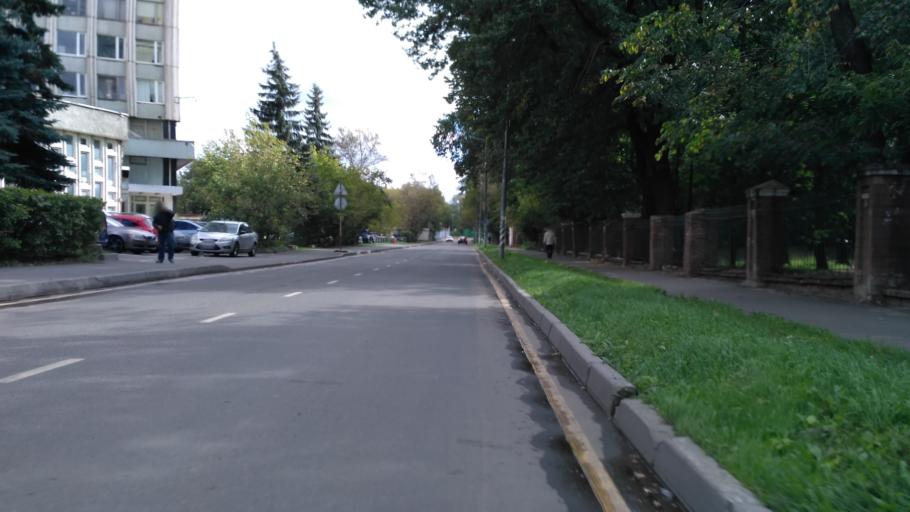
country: RU
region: Moscow
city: Sokol'niki
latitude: 55.8105
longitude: 37.6548
